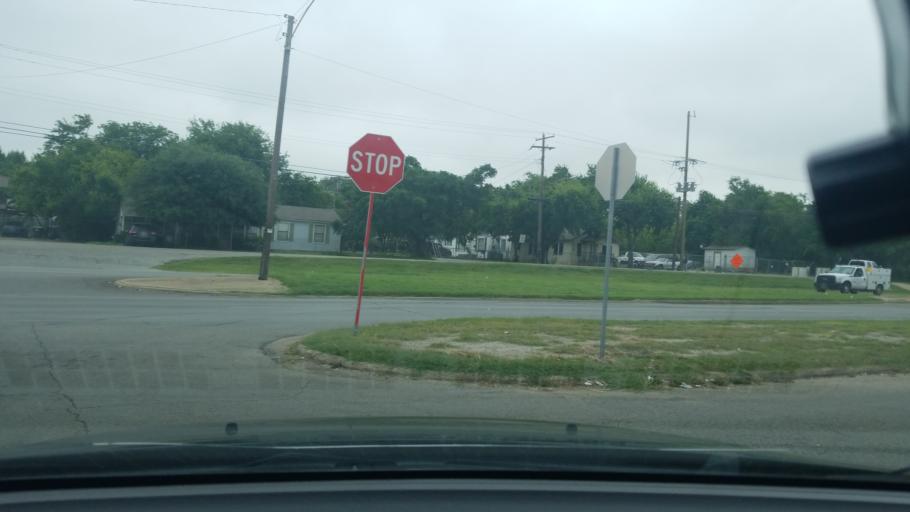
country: US
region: Texas
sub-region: Dallas County
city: Balch Springs
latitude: 32.7707
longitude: -96.6904
